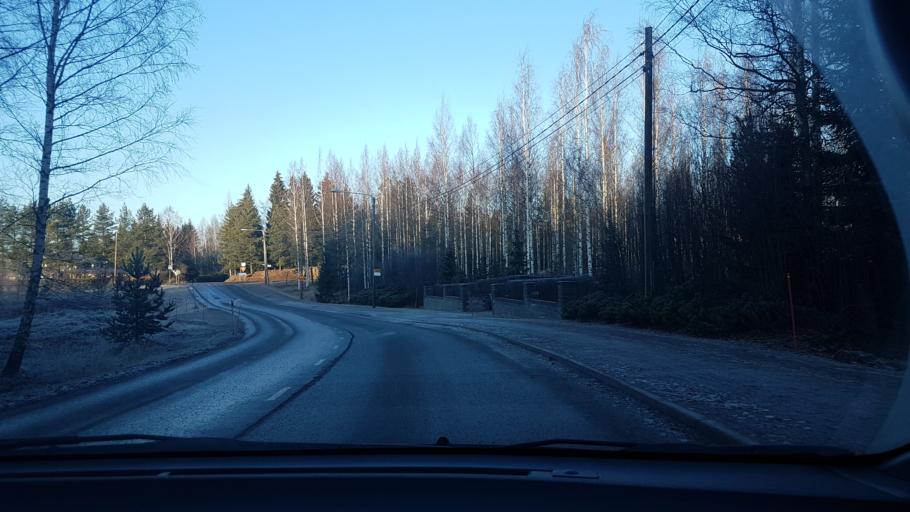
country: FI
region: Uusimaa
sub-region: Helsinki
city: Tuusula
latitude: 60.3777
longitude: 25.0030
